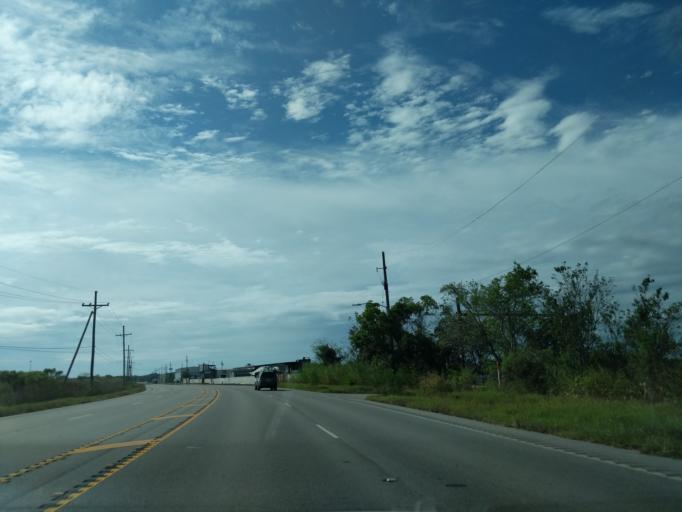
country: US
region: Louisiana
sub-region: Saint Tammany Parish
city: Eden Isle
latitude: 30.0769
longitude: -89.8457
